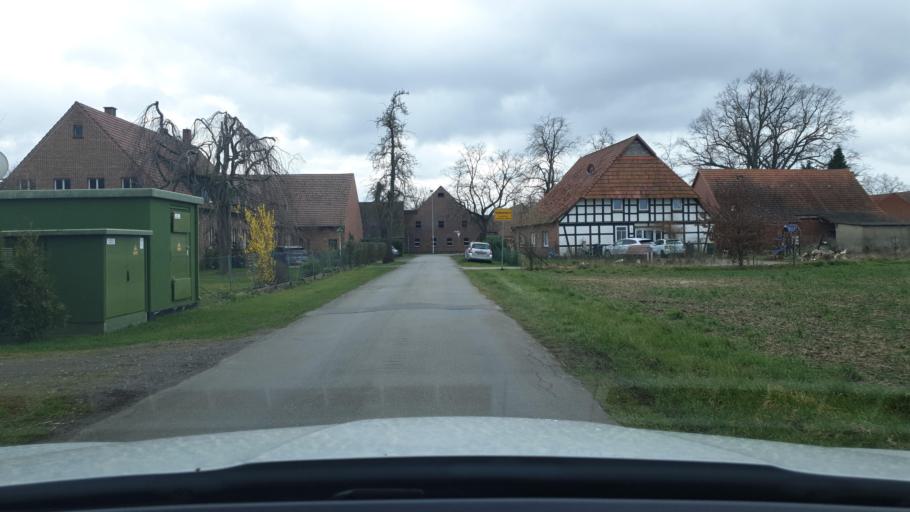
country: DE
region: North Rhine-Westphalia
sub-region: Regierungsbezirk Detmold
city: Hille
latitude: 52.3217
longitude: 8.7947
